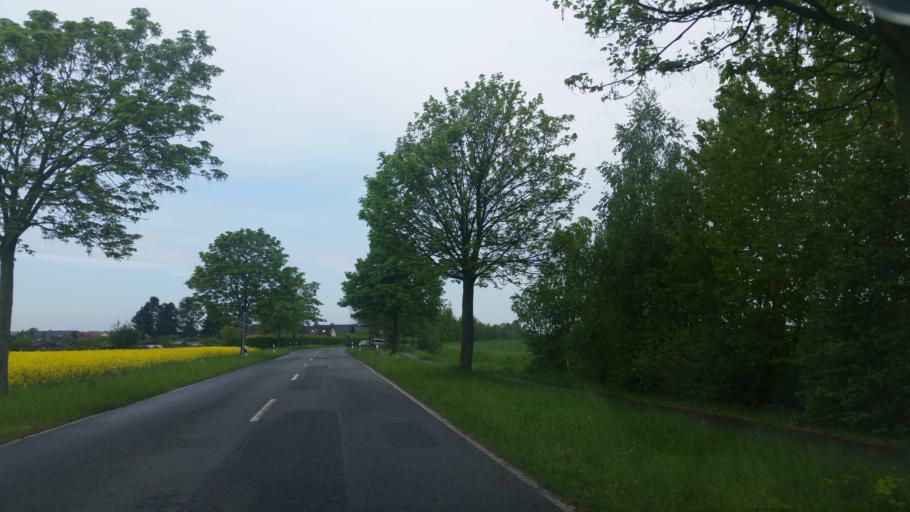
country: DE
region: Lower Saxony
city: Vordorf
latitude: 52.3223
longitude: 10.5669
